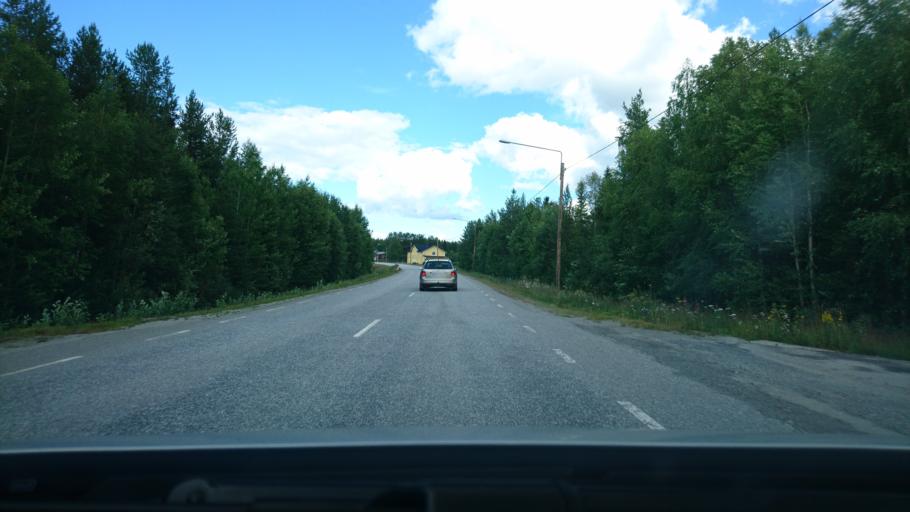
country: SE
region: Vaesterbotten
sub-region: Asele Kommun
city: Asele
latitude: 64.0097
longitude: 17.2859
